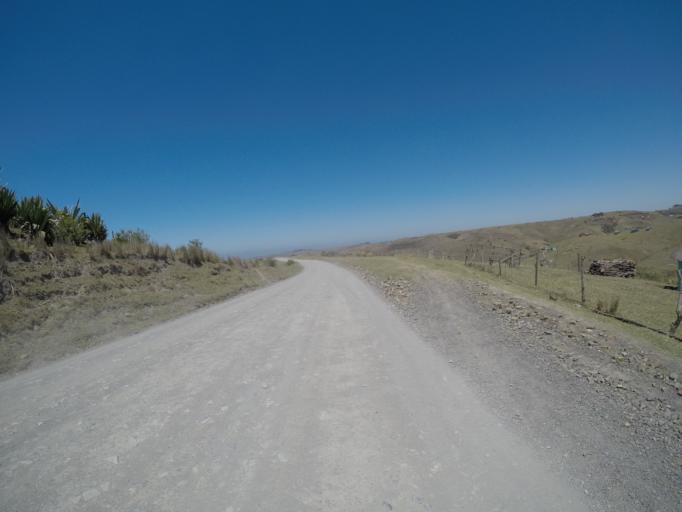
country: ZA
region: Eastern Cape
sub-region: OR Tambo District Municipality
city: Libode
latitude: -31.9913
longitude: 29.0537
